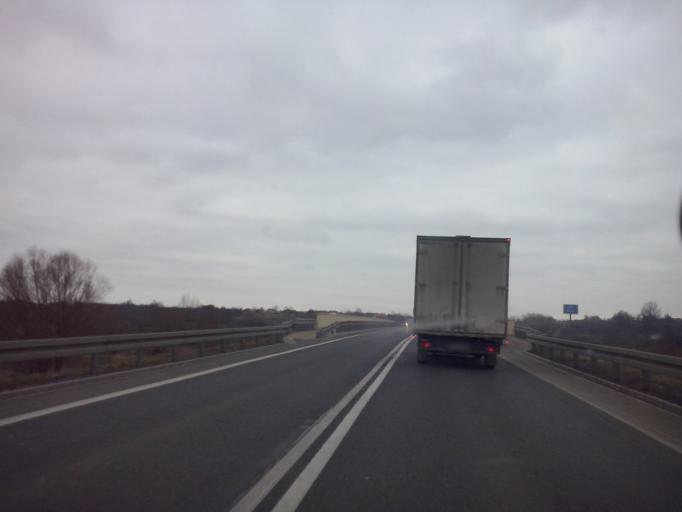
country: PL
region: Subcarpathian Voivodeship
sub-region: Powiat nizanski
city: Zarzecze
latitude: 50.5191
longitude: 22.1871
